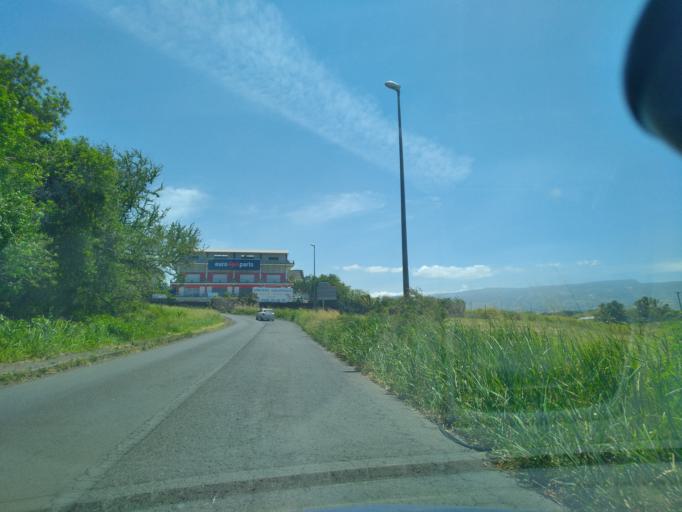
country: RE
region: Reunion
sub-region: Reunion
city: Saint-Pierre
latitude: -21.3231
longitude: 55.4484
